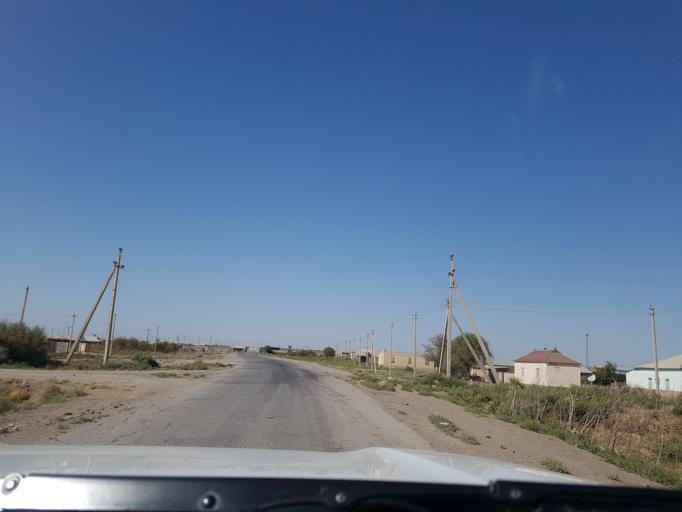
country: IR
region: Razavi Khorasan
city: Sarakhs
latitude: 36.5154
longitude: 61.2525
